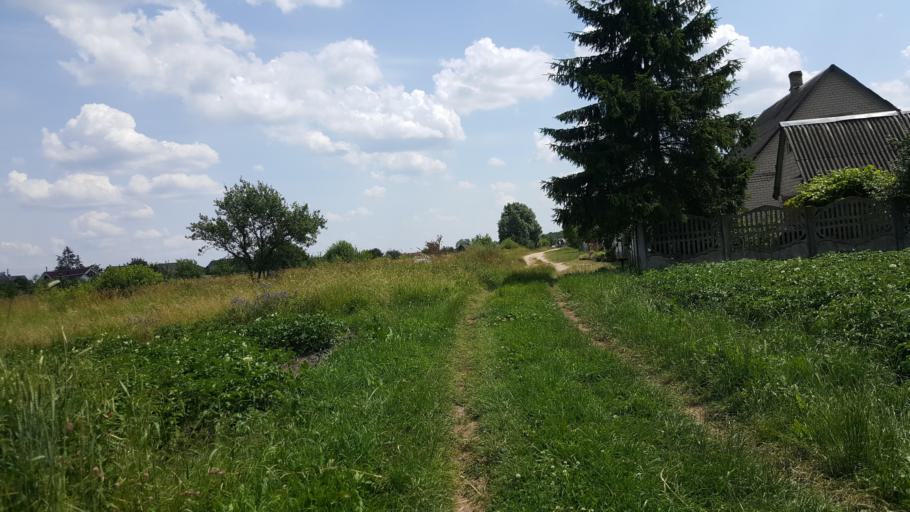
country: BY
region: Brest
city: Kamyanyets
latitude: 52.4041
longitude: 23.7865
